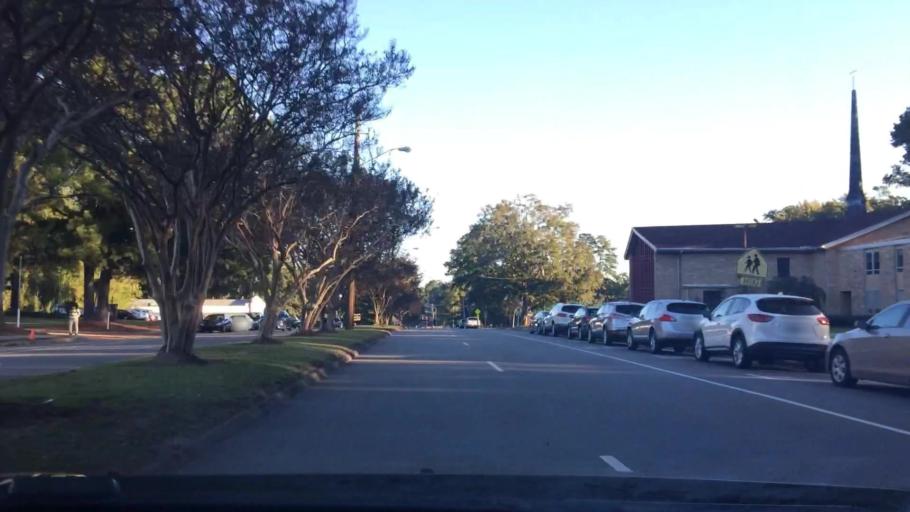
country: US
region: North Carolina
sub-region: Pitt County
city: Greenville
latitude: 35.5992
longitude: -77.3596
